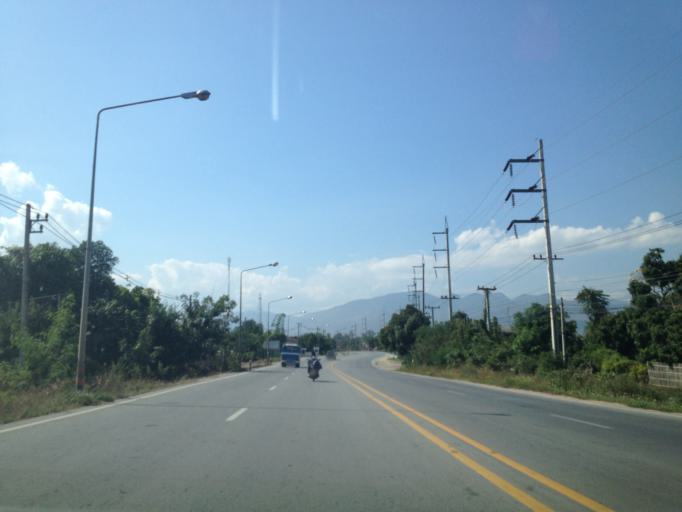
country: TH
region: Chiang Mai
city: Chom Thong
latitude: 18.3083
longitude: 98.6505
